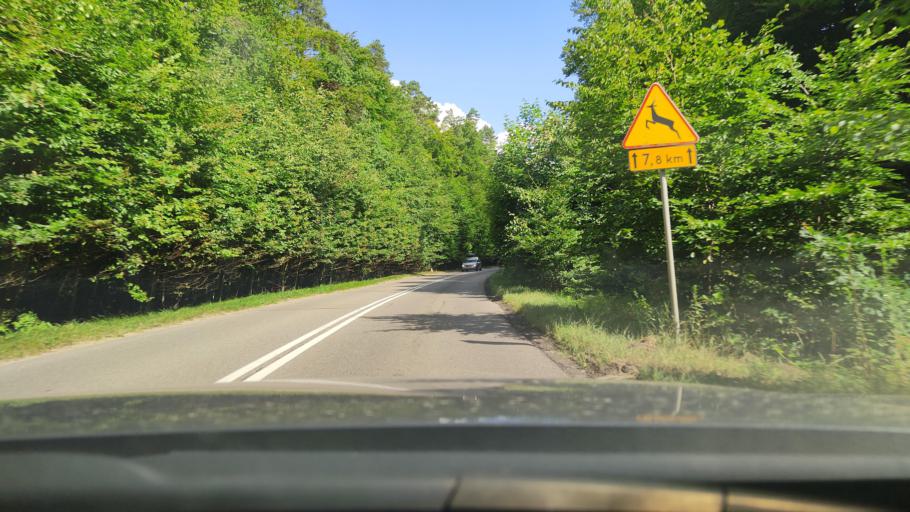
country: PL
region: Pomeranian Voivodeship
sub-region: Powiat wejherowski
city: Wejherowo
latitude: 54.6182
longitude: 18.2216
